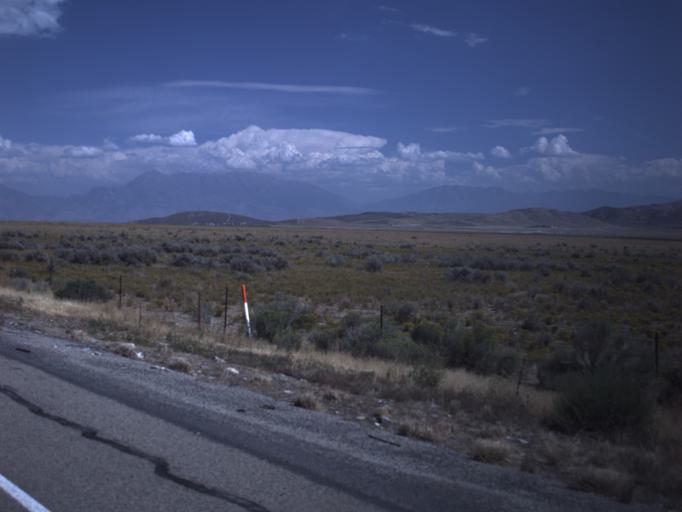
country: US
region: Utah
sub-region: Utah County
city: Eagle Mountain
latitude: 40.3513
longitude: -112.0709
